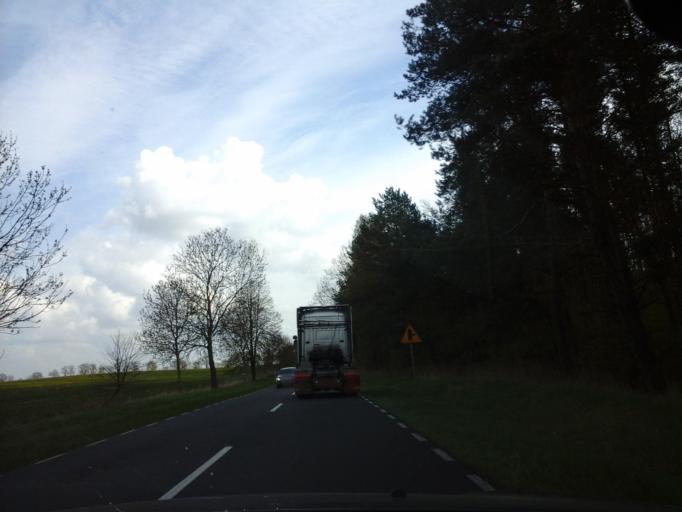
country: PL
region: West Pomeranian Voivodeship
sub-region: Powiat choszczenski
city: Choszczno
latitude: 53.1991
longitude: 15.3512
